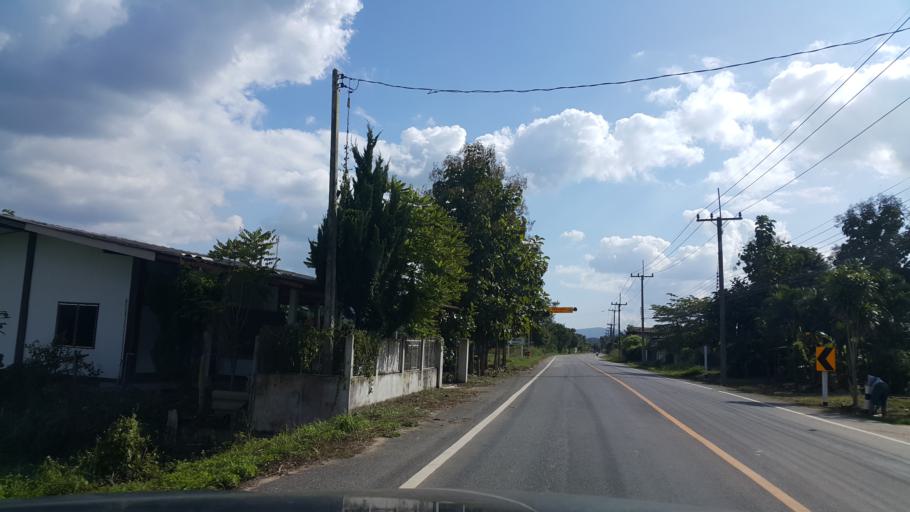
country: TH
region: Lamphun
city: Ban Thi
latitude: 18.6060
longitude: 99.2726
